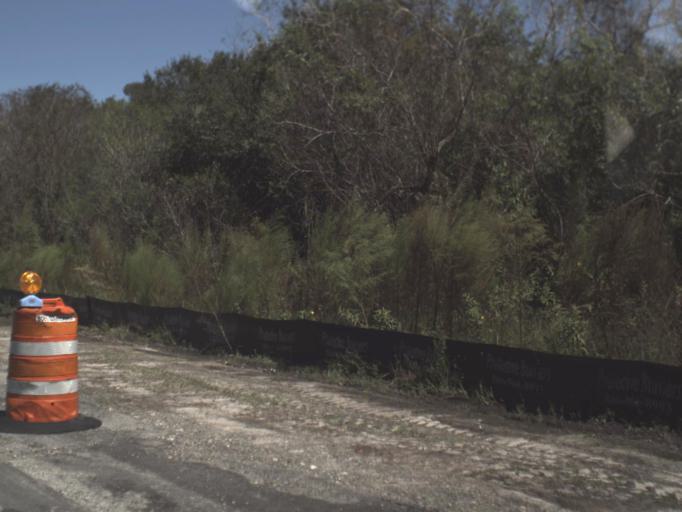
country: US
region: Florida
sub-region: Collier County
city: Lely Resort
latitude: 26.0394
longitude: -81.7002
